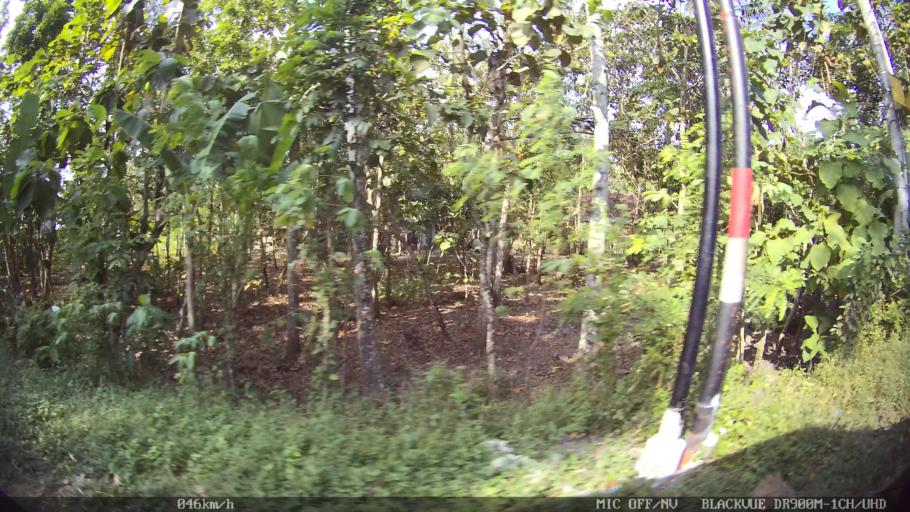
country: ID
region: Daerah Istimewa Yogyakarta
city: Kasihan
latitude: -7.8535
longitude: 110.3189
